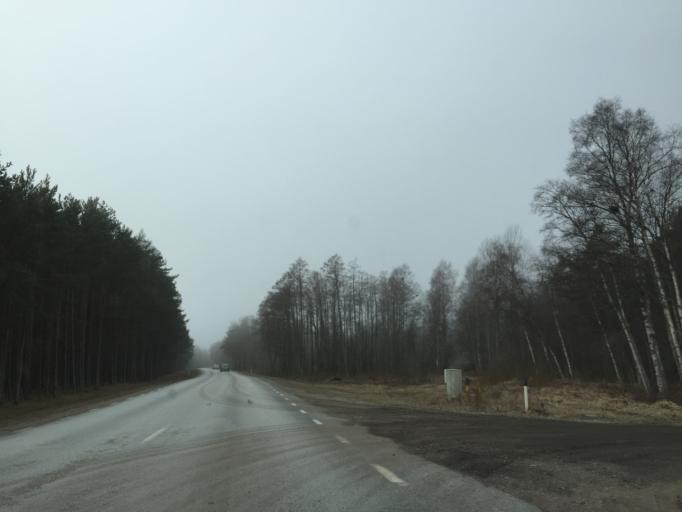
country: EE
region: Saare
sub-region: Kuressaare linn
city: Kuressaare
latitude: 58.2096
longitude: 22.3070
